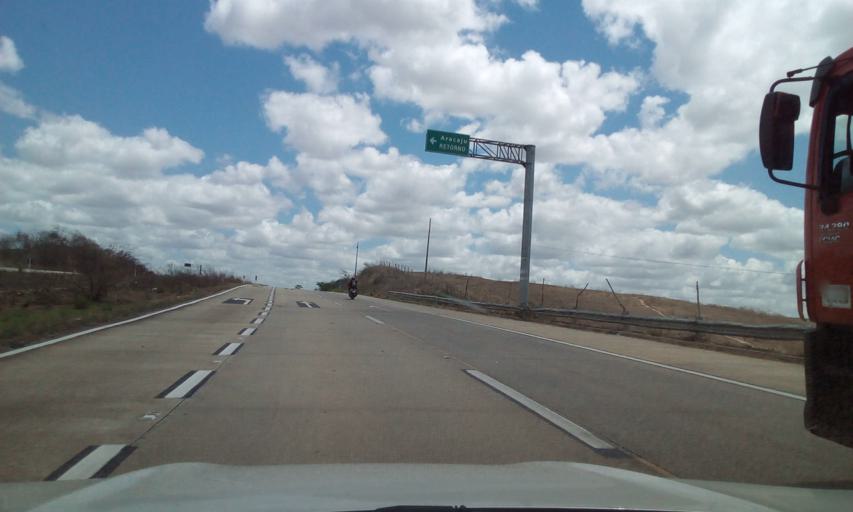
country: BR
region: Alagoas
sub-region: Porto Real Do Colegio
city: Porto Real do Colegio
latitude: -10.1641
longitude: -36.8165
